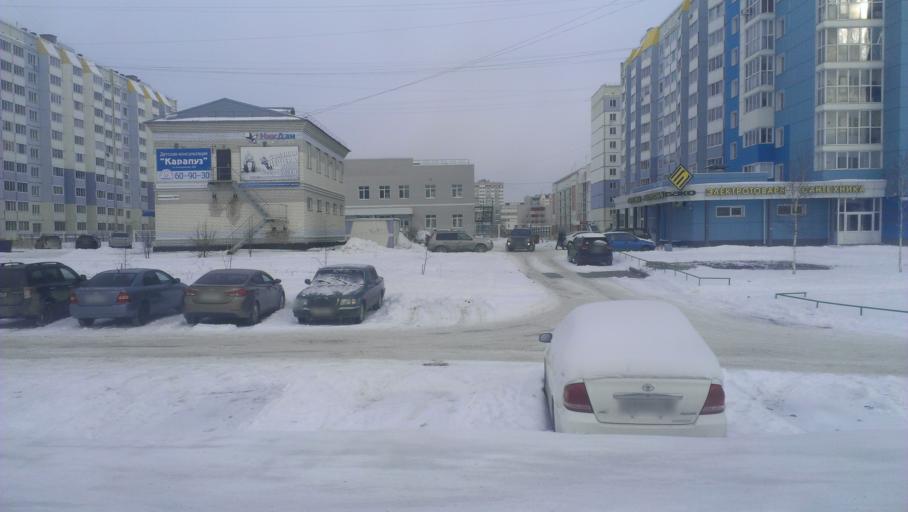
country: RU
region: Altai Krai
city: Novosilikatnyy
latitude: 53.3277
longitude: 83.6870
